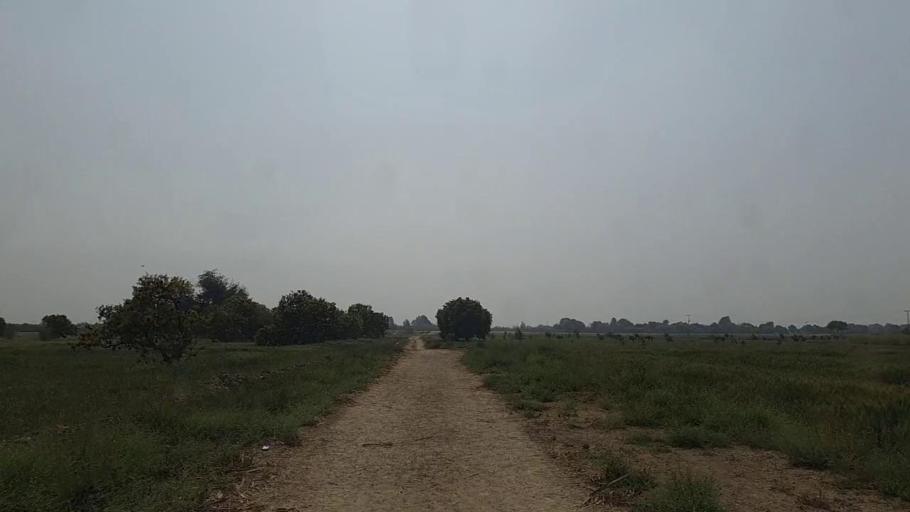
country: PK
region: Sindh
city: Naukot
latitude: 24.8318
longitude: 69.3994
